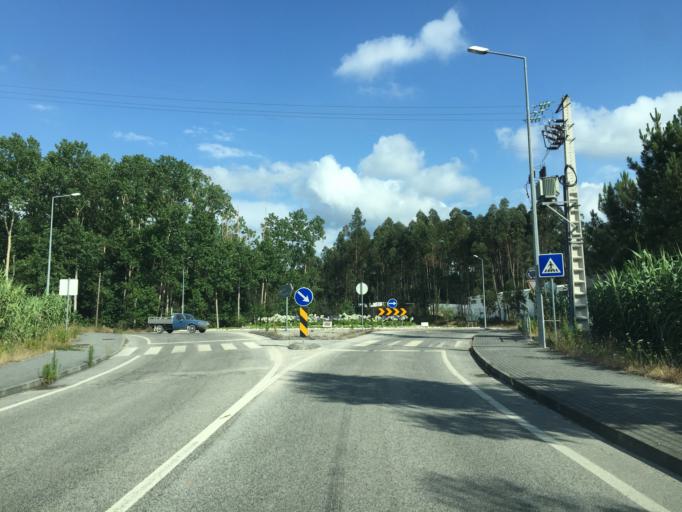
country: PT
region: Leiria
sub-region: Leiria
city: Monte Redondo
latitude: 39.9414
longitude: -8.7949
